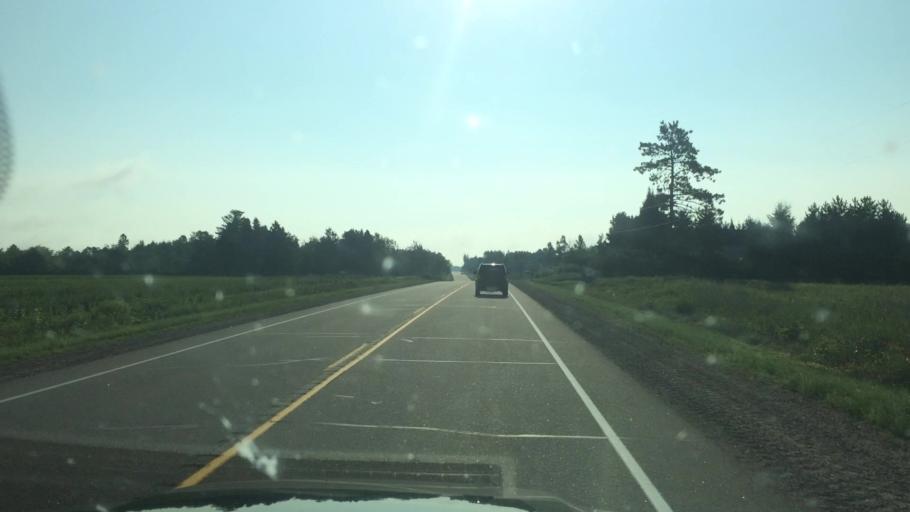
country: US
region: Wisconsin
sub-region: Langlade County
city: Antigo
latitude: 45.1399
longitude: -89.2228
